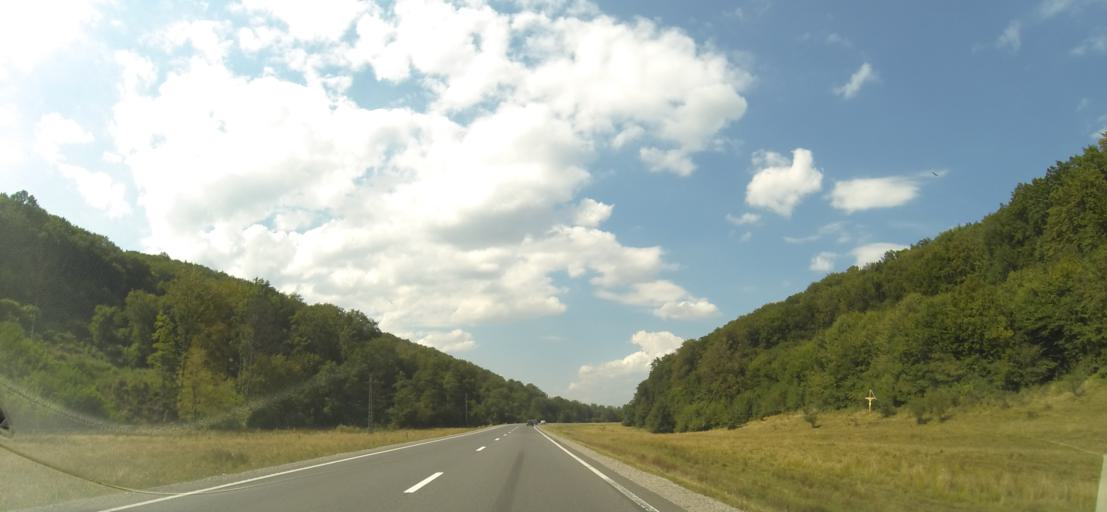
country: RO
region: Brasov
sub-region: Comuna Sinca Veche
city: Persani
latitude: 45.7591
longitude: 25.2388
